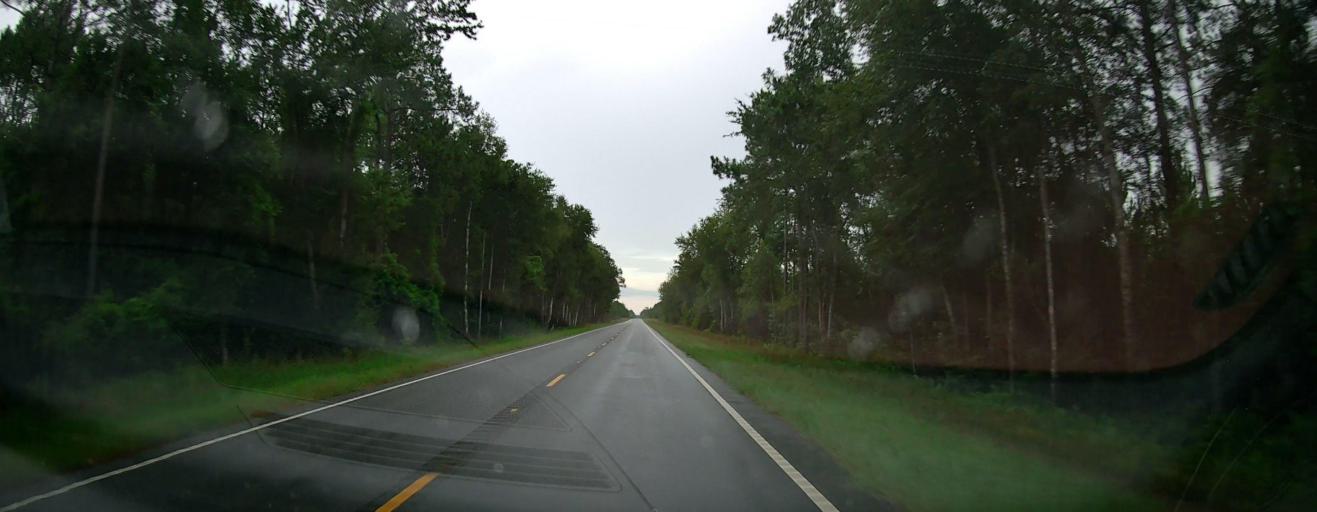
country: US
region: Georgia
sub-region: Brantley County
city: Nahunta
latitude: 31.3411
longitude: -81.8332
